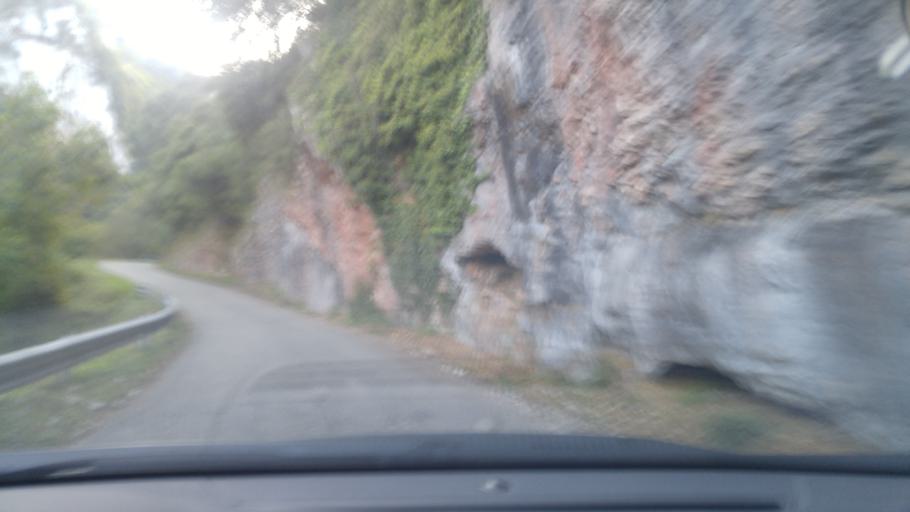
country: ES
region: Asturias
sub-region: Province of Asturias
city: Proaza
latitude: 43.2476
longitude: -6.0301
